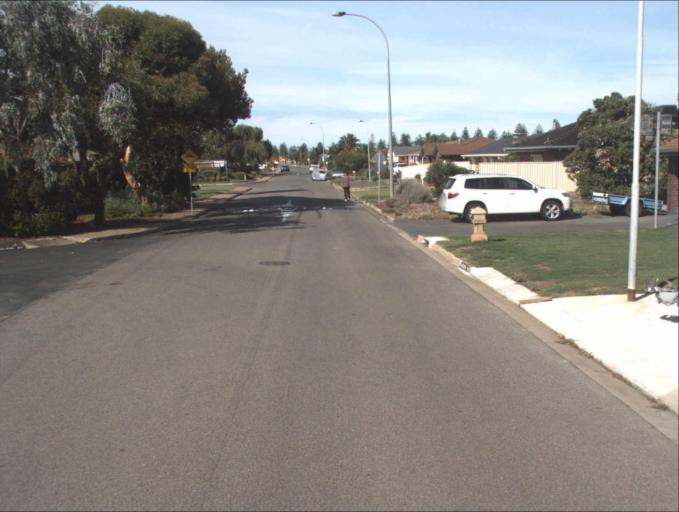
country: AU
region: South Australia
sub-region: Port Adelaide Enfield
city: Birkenhead
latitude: -34.7812
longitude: 138.4937
